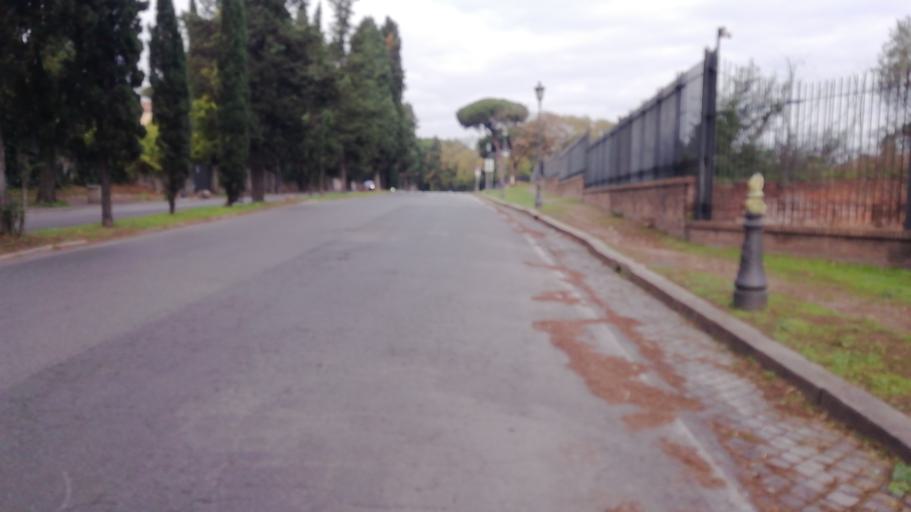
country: IT
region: Latium
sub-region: Citta metropolitana di Roma Capitale
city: Rome
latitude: 41.8778
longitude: 12.4915
